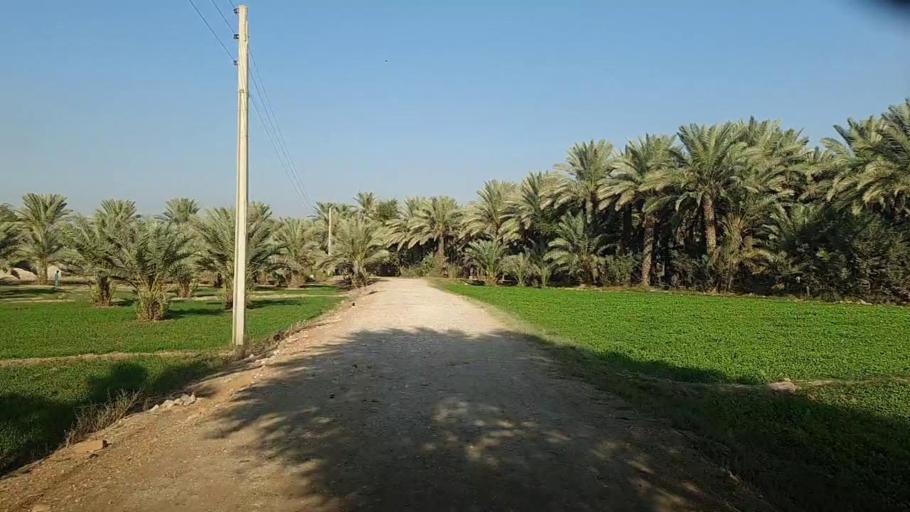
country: PK
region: Sindh
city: Ranipur
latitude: 27.2545
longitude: 68.5514
